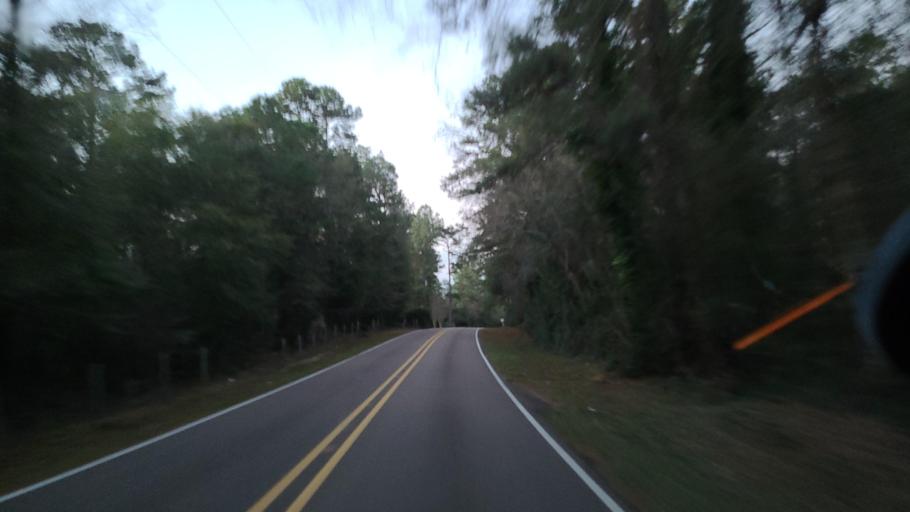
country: US
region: Mississippi
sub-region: Forrest County
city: Hattiesburg
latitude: 31.2378
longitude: -89.2421
